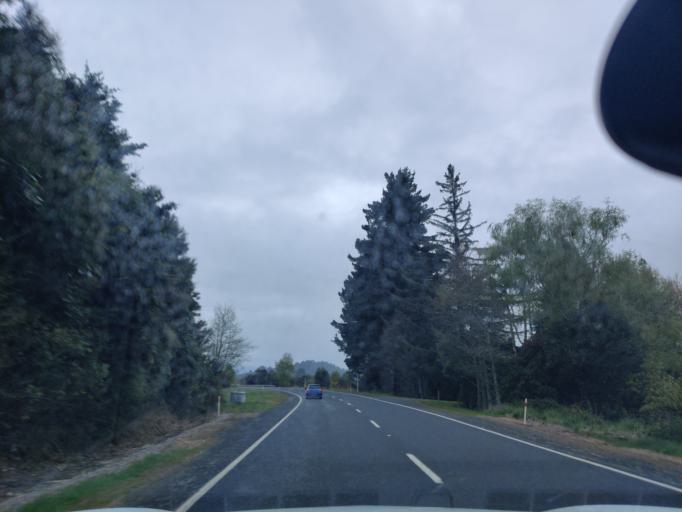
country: NZ
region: Waikato
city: Turangi
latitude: -38.9770
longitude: 175.7718
